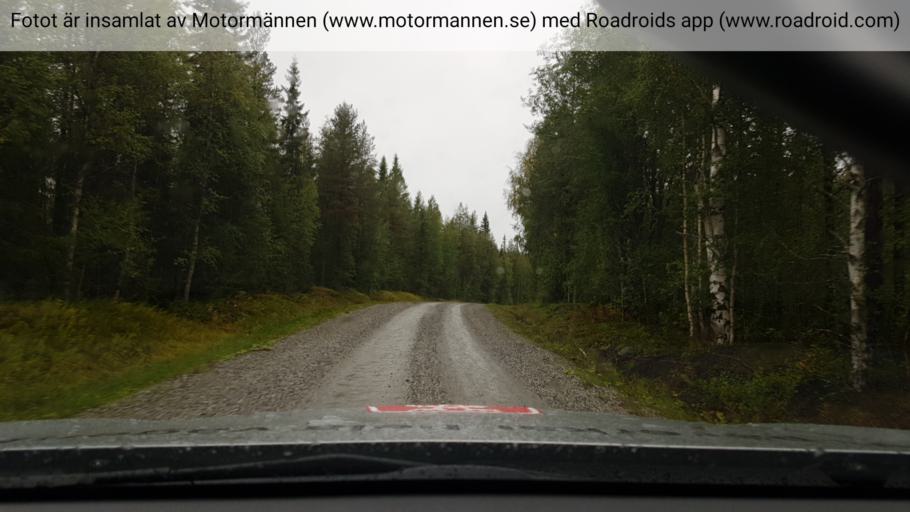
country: SE
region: Vaesterbotten
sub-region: Asele Kommun
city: Asele
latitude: 63.9961
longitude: 17.6059
